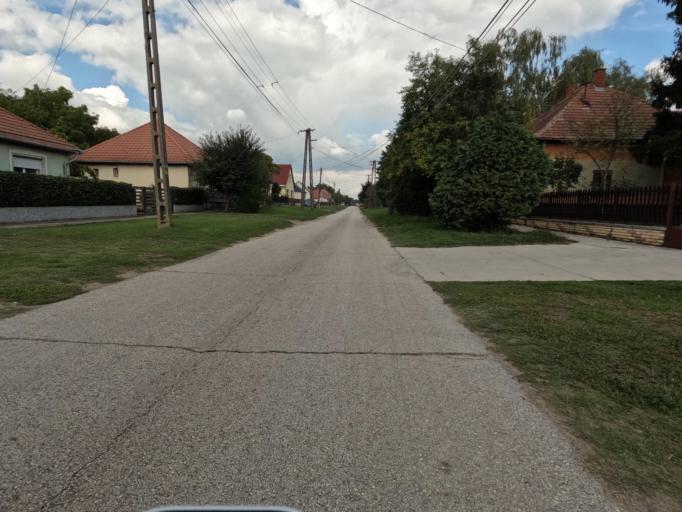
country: HU
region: Tolna
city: Tengelic
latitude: 46.5213
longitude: 18.7018
